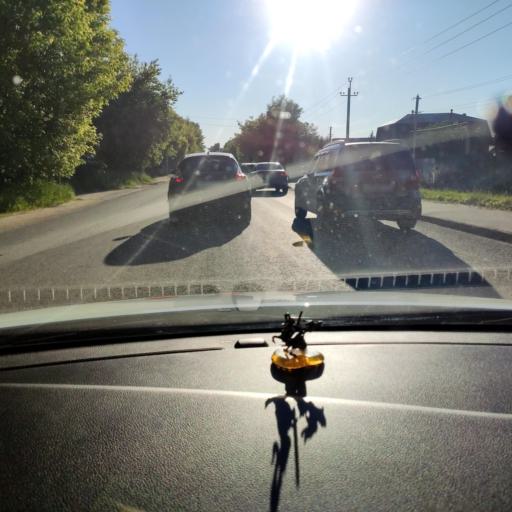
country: RU
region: Tatarstan
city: Verkhniy Uslon
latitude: 55.8000
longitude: 49.0257
